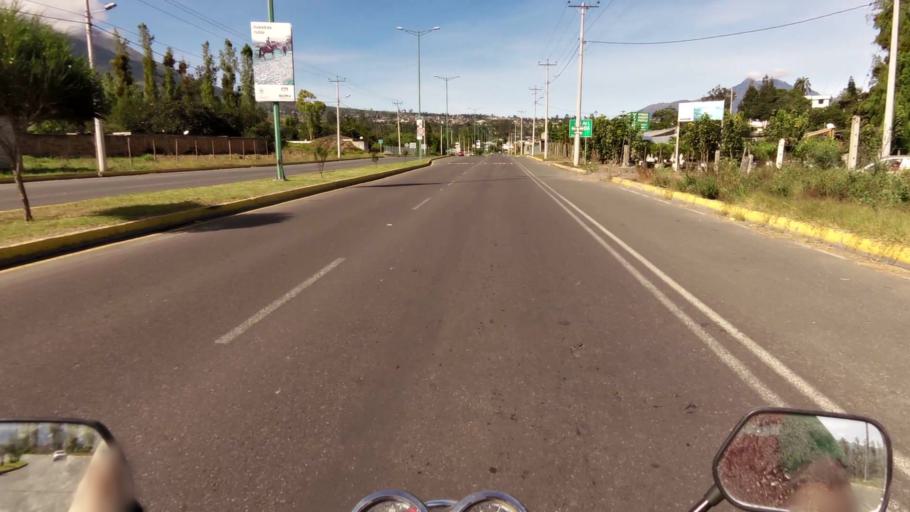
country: EC
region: Imbabura
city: Ibarra
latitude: 0.3321
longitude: -78.1474
